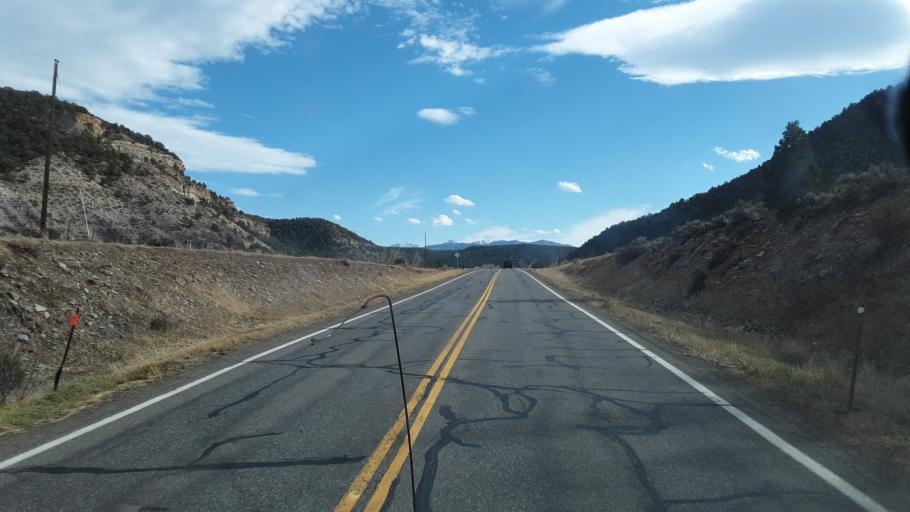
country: US
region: Colorado
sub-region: Montrose County
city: Montrose
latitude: 38.2717
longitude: -107.7674
